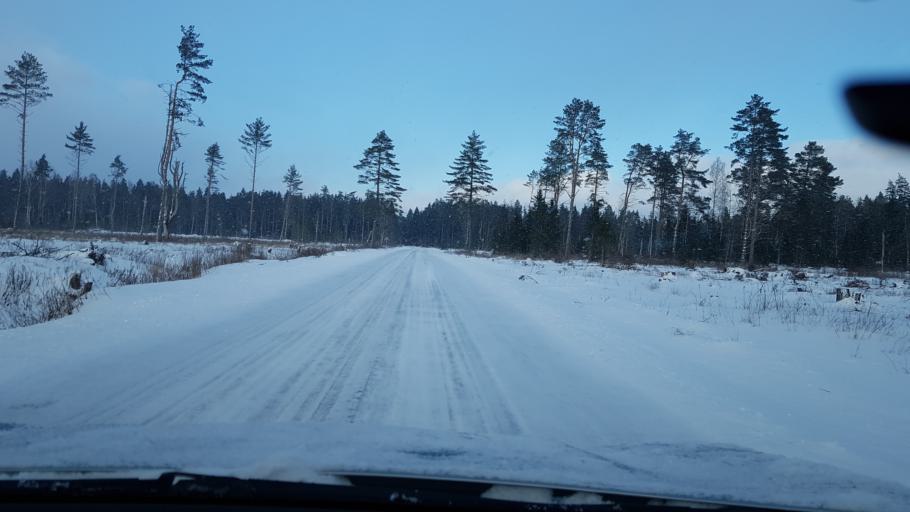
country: EE
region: Harju
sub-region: Nissi vald
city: Turba
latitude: 59.2053
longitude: 24.1405
